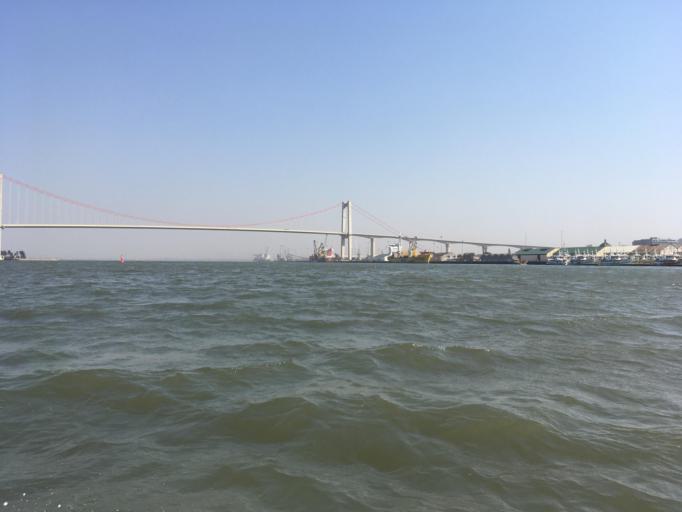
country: MZ
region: Maputo City
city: Maputo
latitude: -25.9790
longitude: 32.5670
